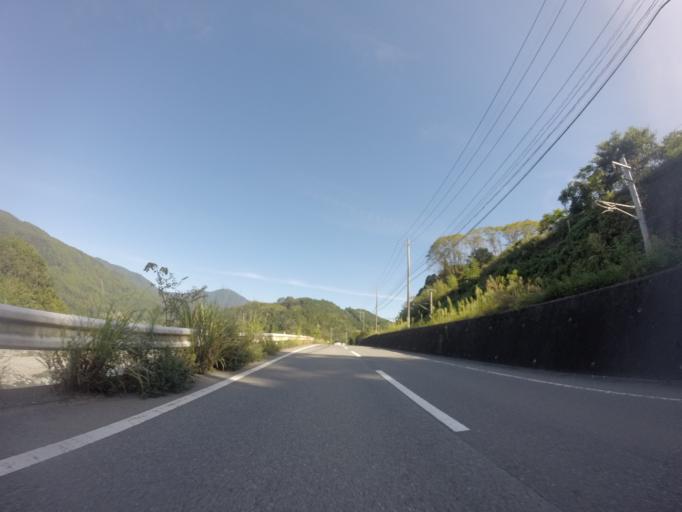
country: JP
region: Shizuoka
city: Fujinomiya
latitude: 35.3391
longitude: 138.4496
